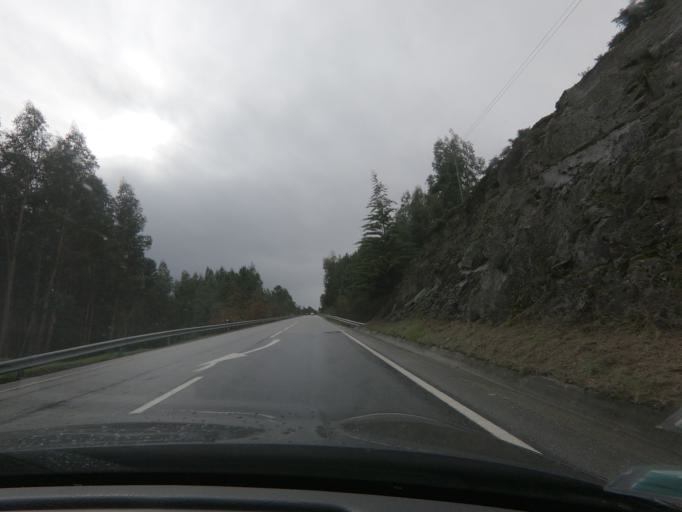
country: PT
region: Braga
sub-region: Celorico de Basto
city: Celorico de Basto
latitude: 41.3516
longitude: -8.0147
